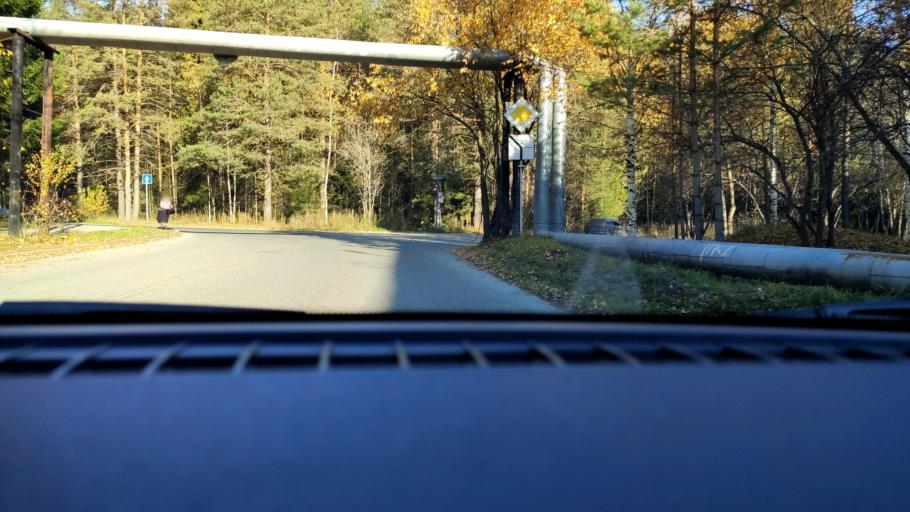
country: RU
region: Perm
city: Perm
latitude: 58.0545
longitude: 56.2302
